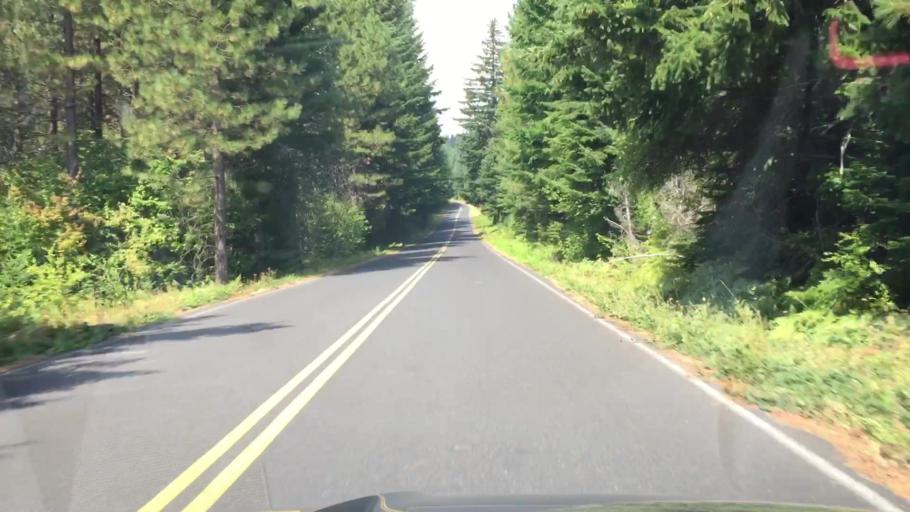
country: US
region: Washington
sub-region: Klickitat County
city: White Salmon
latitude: 46.0387
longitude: -121.5473
